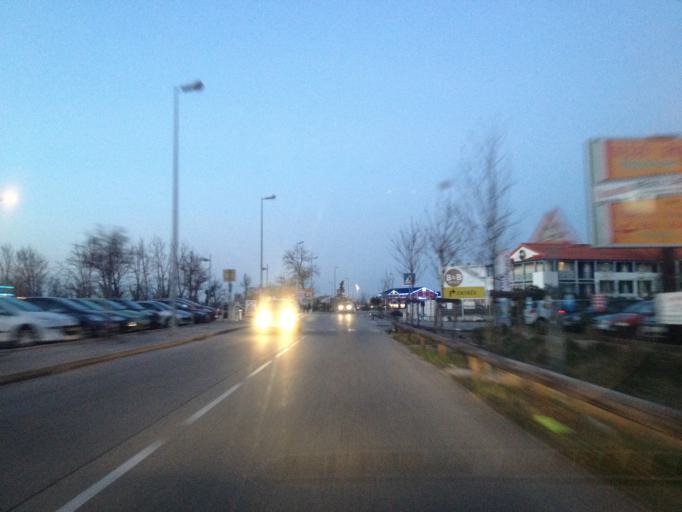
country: FR
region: Provence-Alpes-Cote d'Azur
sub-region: Departement du Vaucluse
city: Le Pontet
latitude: 43.9778
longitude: 4.8718
